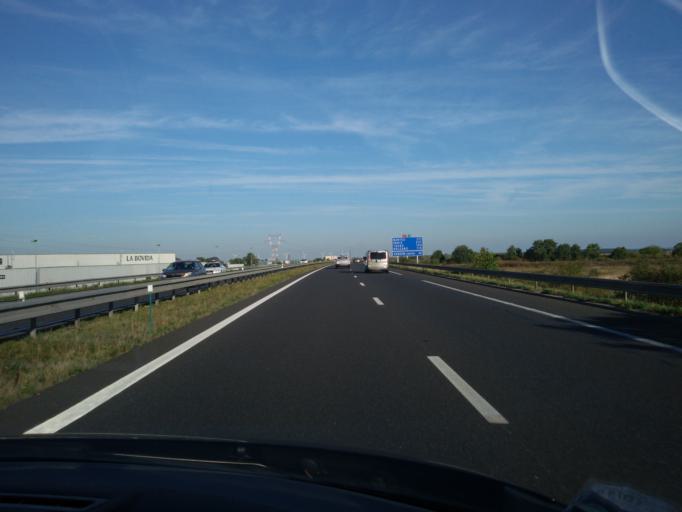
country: FR
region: Centre
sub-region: Departement du Cher
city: La Chapelle-Saint-Ursin
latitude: 47.0471
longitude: 2.3282
